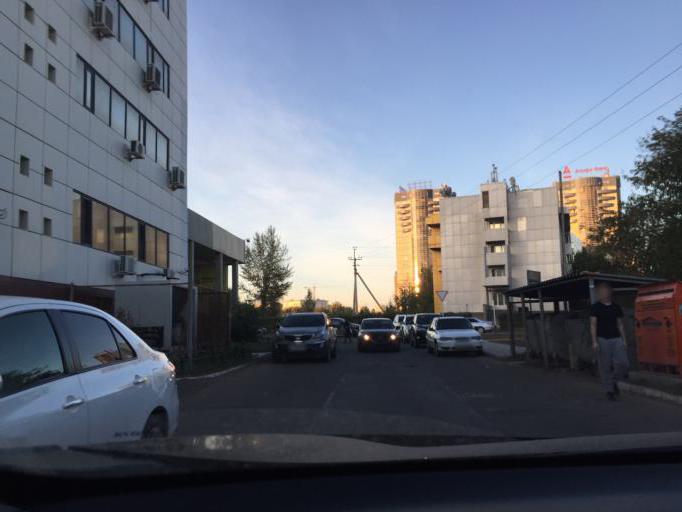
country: KZ
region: Astana Qalasy
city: Astana
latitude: 51.1436
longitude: 71.4212
